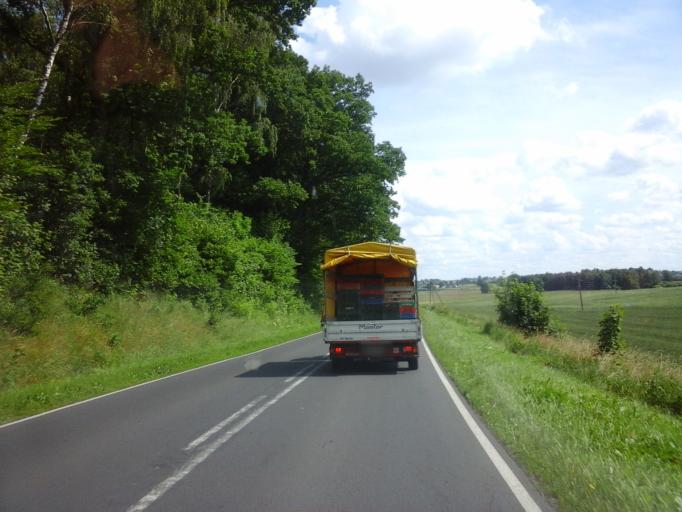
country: PL
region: West Pomeranian Voivodeship
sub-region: Powiat swidwinski
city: Swidwin
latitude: 53.8064
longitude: 15.7692
